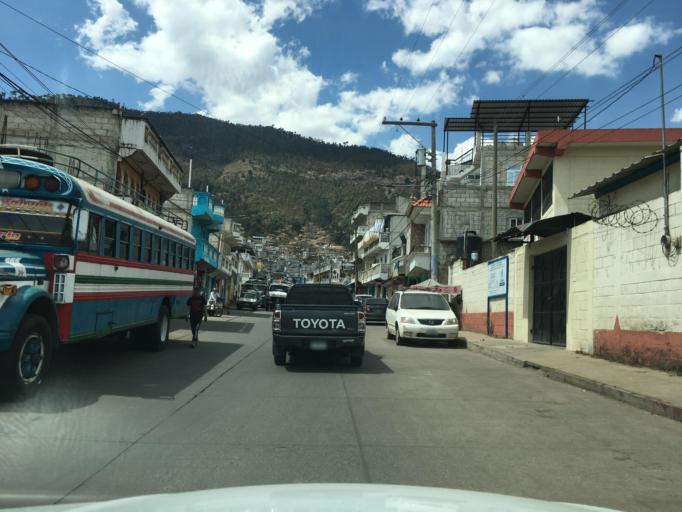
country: GT
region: Totonicapan
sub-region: Municipio de San Andres Xecul
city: San Andres Xecul
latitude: 14.9050
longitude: -91.4795
